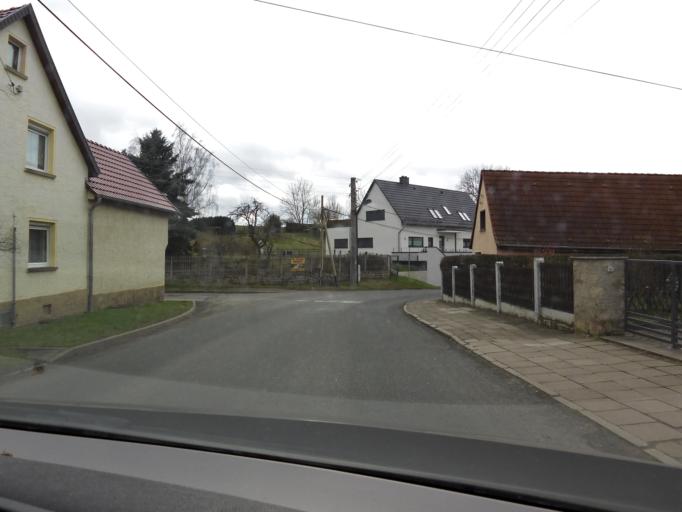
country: DE
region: Thuringia
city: Niederrossla
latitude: 51.0025
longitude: 11.4900
